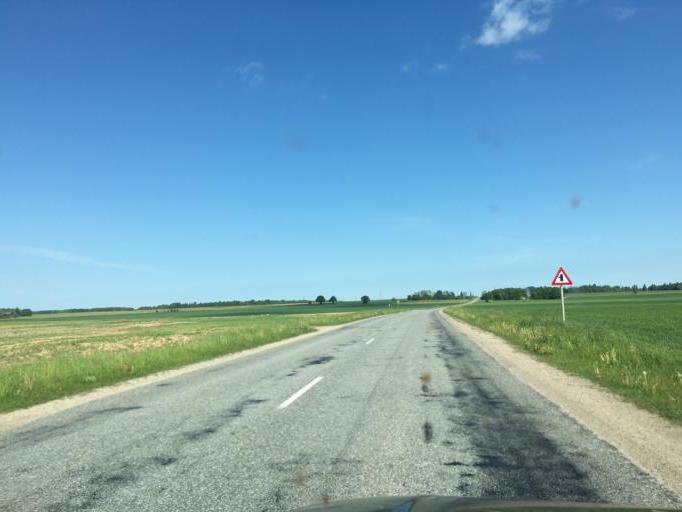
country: LV
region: Talsu Rajons
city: Valdemarpils
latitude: 57.3473
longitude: 22.4998
